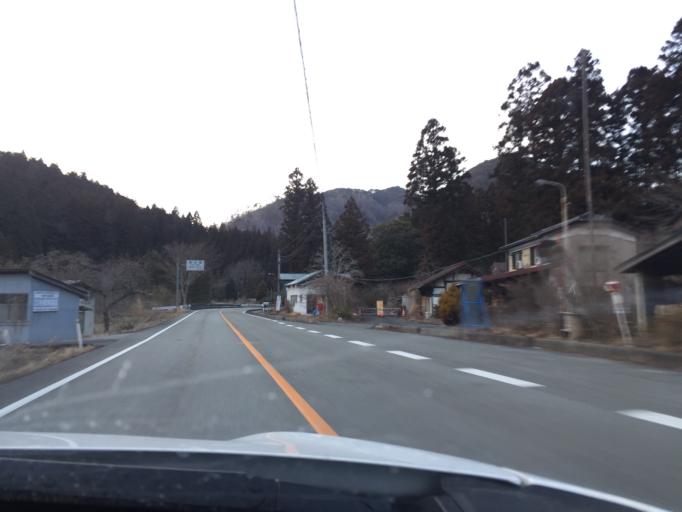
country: JP
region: Fukushima
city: Namie
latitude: 37.5057
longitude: 140.9116
